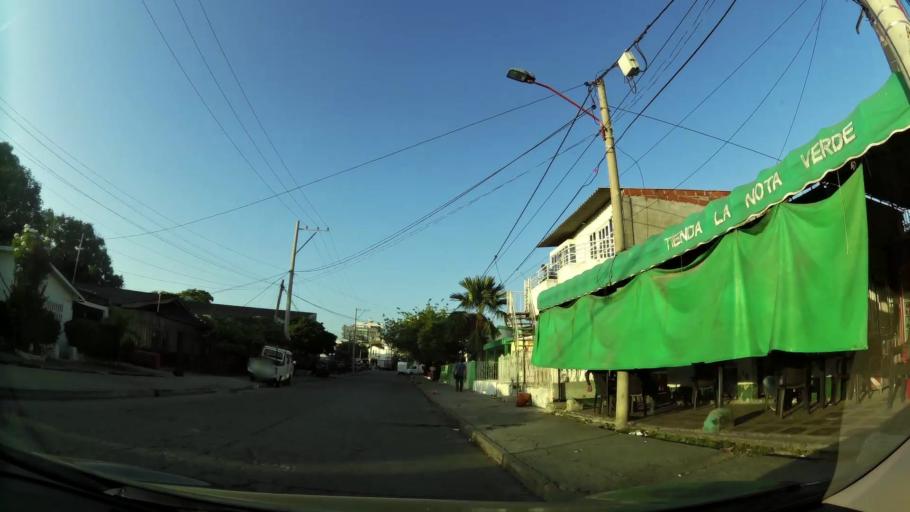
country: CO
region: Bolivar
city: Cartagena
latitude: 10.3903
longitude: -75.5193
